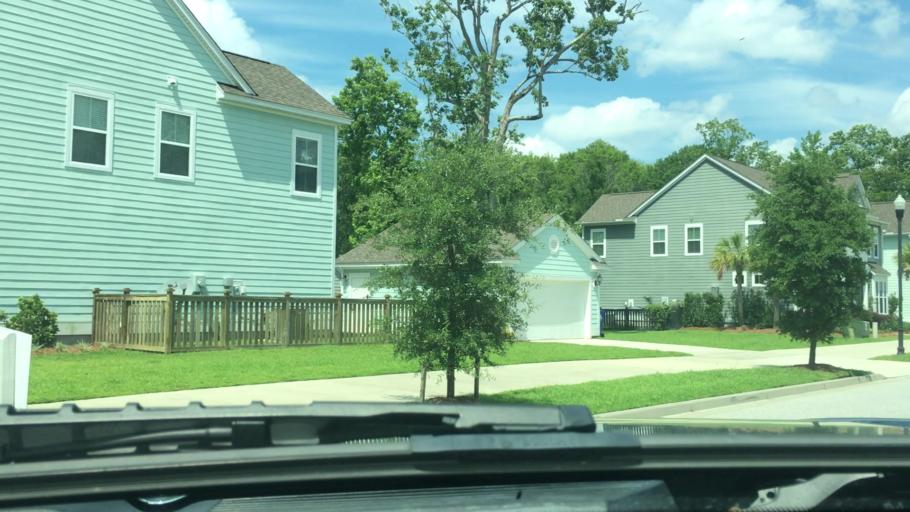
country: US
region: South Carolina
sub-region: Charleston County
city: Shell Point
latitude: 32.8090
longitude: -80.0718
